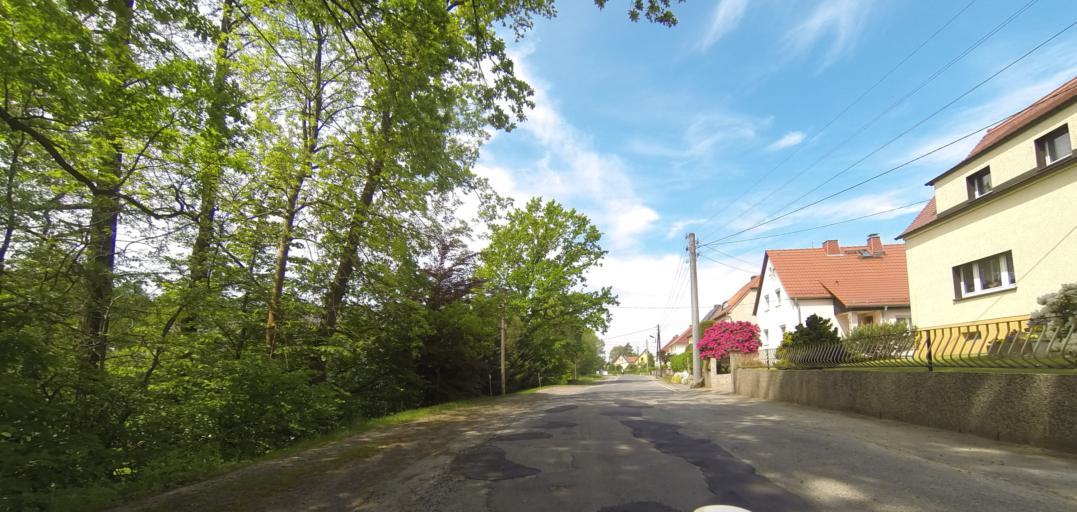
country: DE
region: Saxony
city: Grossharthau
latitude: 51.0971
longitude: 14.0510
